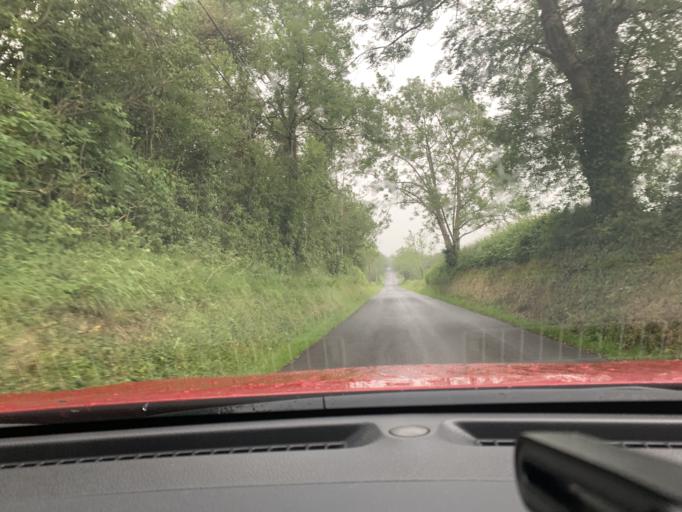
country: GB
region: Northern Ireland
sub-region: Fermanagh District
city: Enniskillen
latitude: 54.2861
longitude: -7.7275
